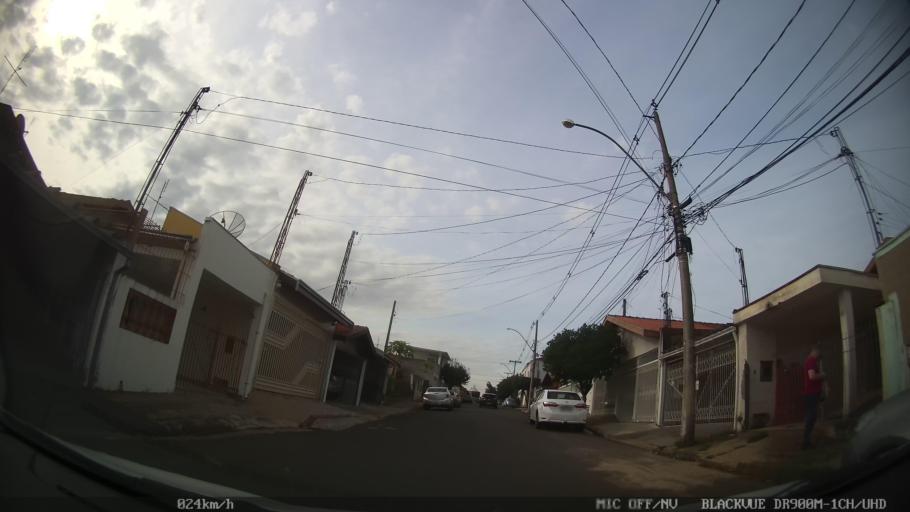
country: BR
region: Sao Paulo
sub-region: Piracicaba
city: Piracicaba
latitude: -22.7412
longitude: -47.6262
